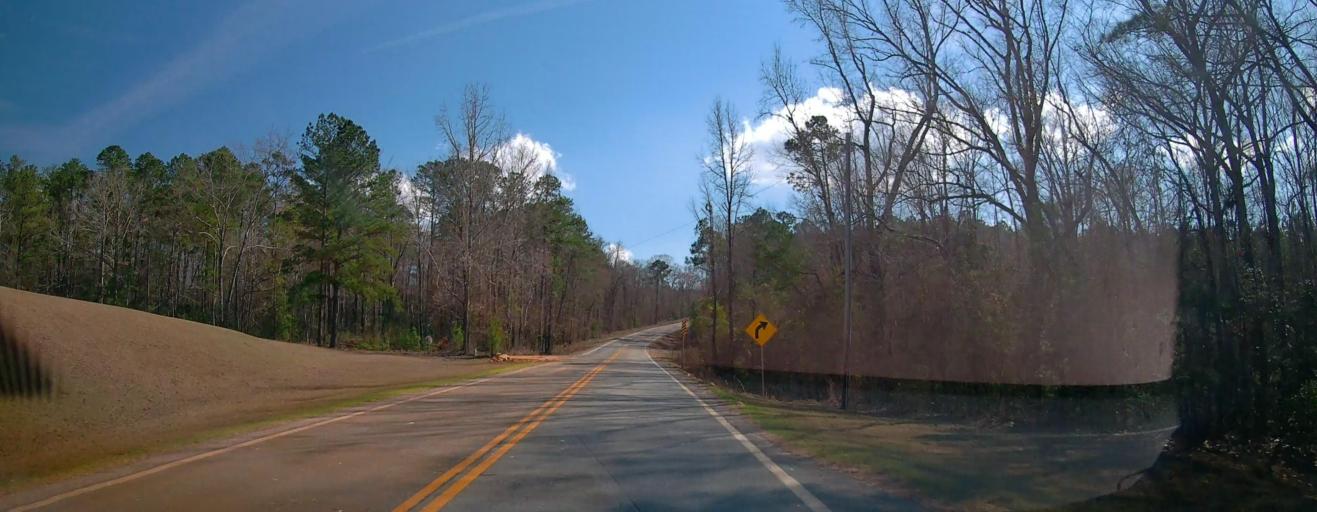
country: US
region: Georgia
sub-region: Wilkinson County
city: Gordon
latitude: 32.8133
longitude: -83.3240
